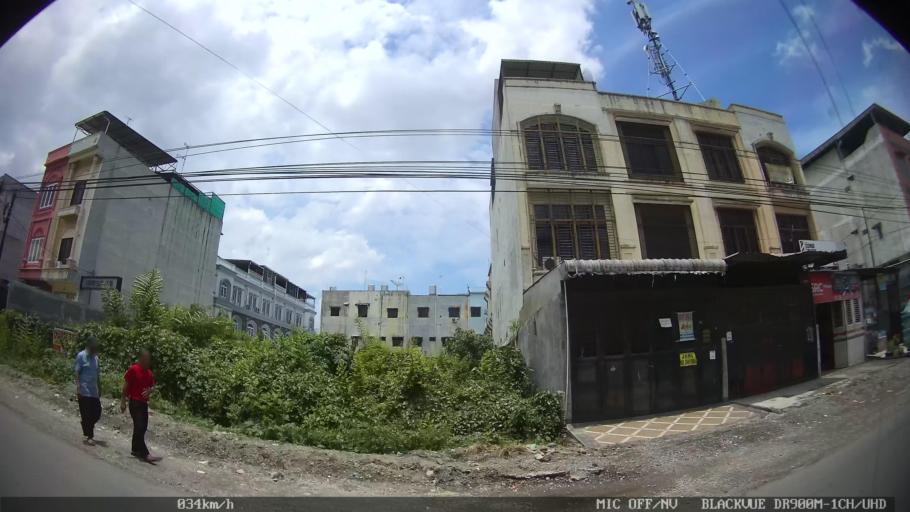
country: ID
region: North Sumatra
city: Medan
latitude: 3.6167
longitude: 98.6847
